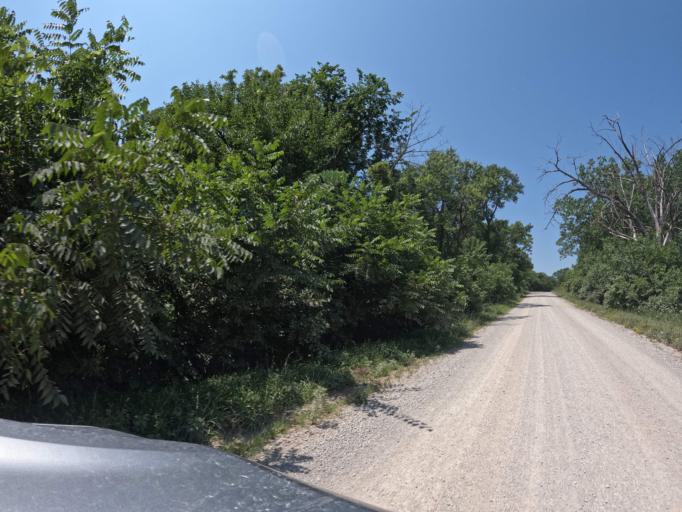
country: US
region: Iowa
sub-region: Appanoose County
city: Centerville
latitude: 40.7767
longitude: -92.9502
